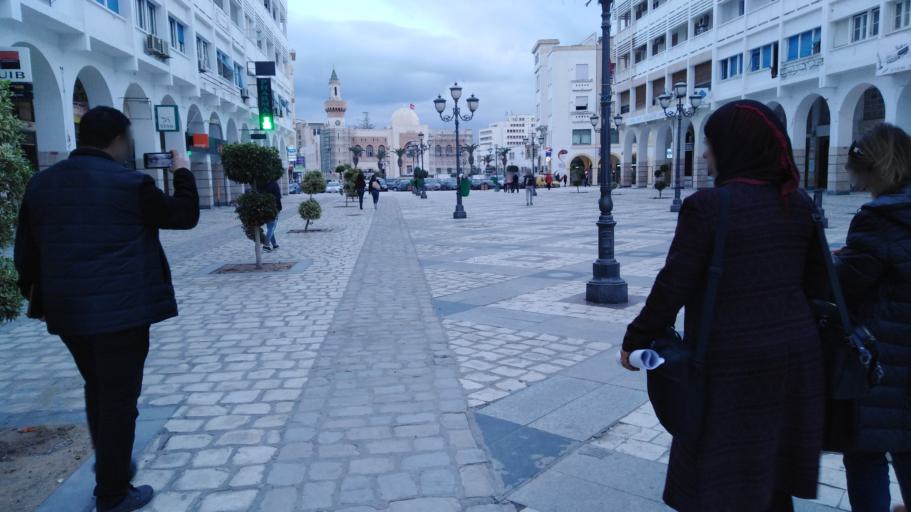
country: TN
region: Safaqis
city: Sfax
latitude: 34.7338
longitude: 10.7630
